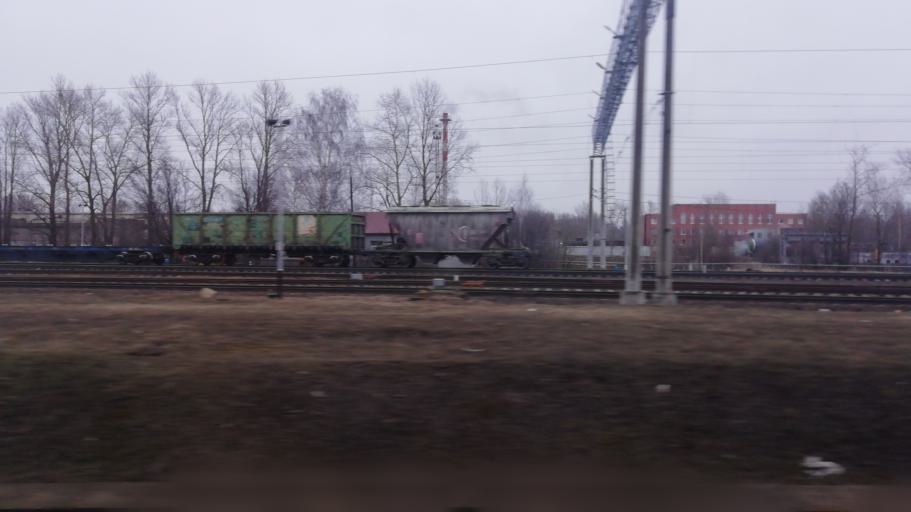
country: RU
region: St.-Petersburg
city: Kupchino
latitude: 59.8837
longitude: 30.3467
